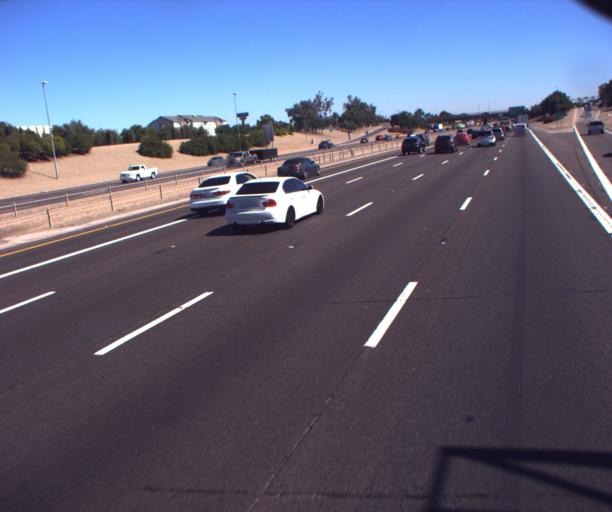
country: US
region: Arizona
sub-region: Maricopa County
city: Glendale
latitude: 33.4620
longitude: -112.1569
